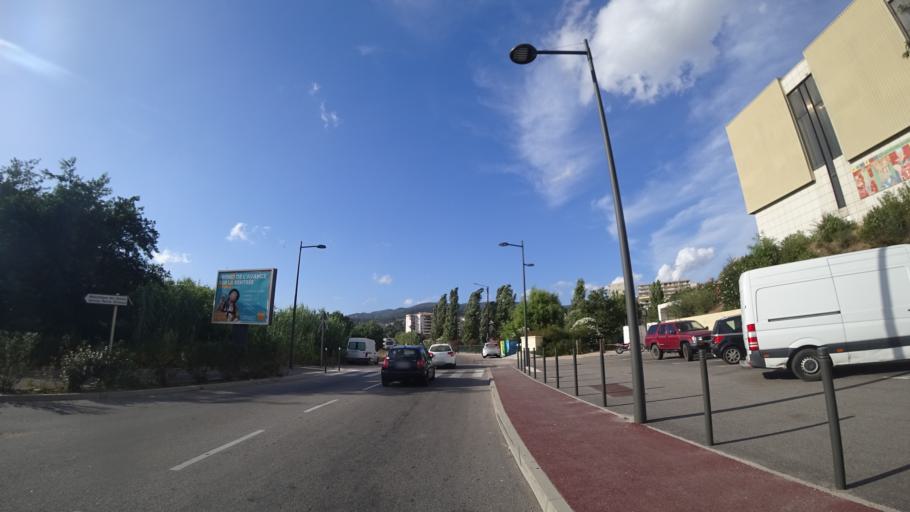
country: FR
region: Corsica
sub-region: Departement de la Corse-du-Sud
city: Ajaccio
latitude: 41.9364
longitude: 8.7427
